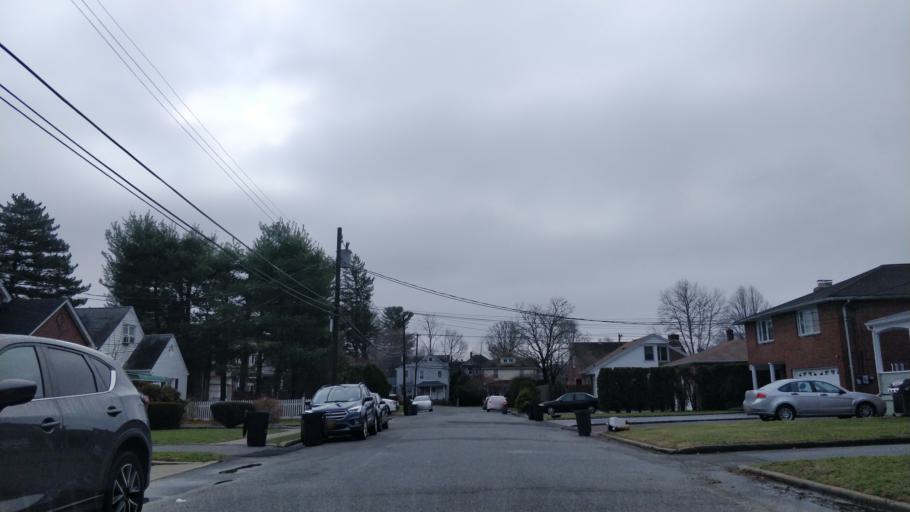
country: US
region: New York
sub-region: Nassau County
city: Glen Cove
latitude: 40.8603
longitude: -73.6139
